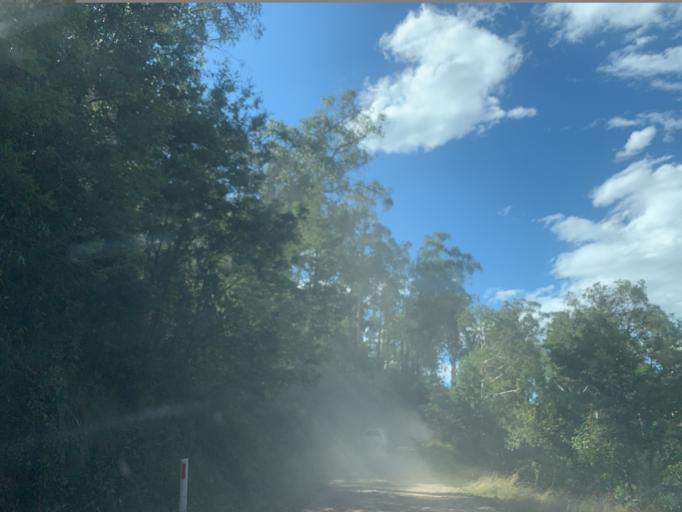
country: AU
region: Victoria
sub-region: Mansfield
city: Mansfield
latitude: -37.0936
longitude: 146.5185
